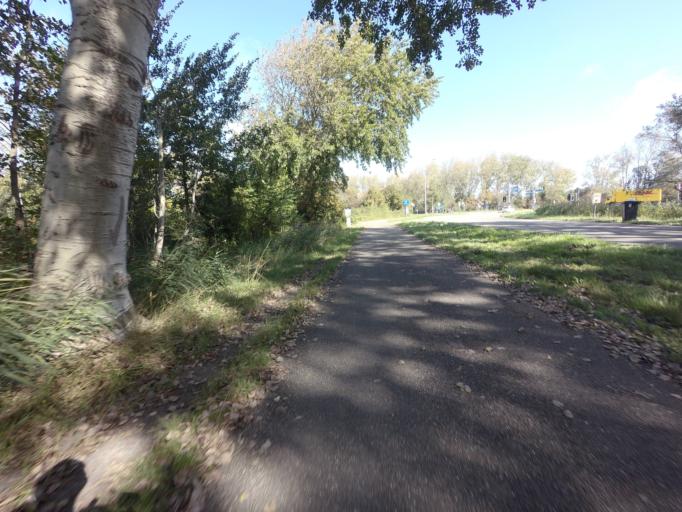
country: NL
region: Zeeland
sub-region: Gemeente Vlissingen
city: Vlissingen
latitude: 51.4961
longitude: 3.5192
